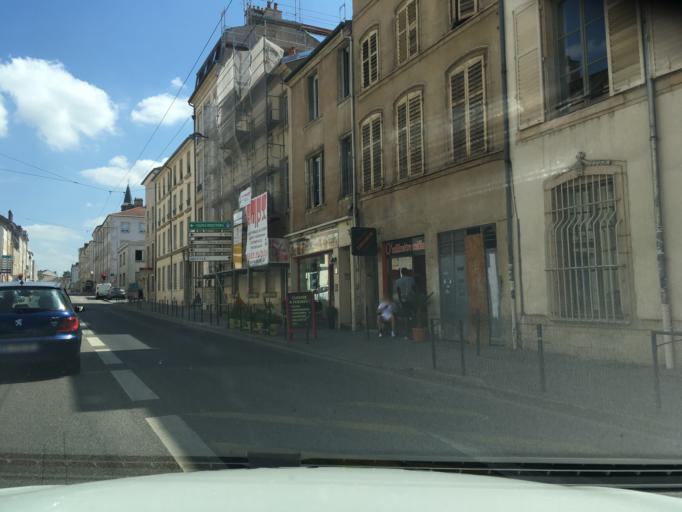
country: FR
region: Lorraine
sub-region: Departement de Meurthe-et-Moselle
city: Nancy
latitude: 48.6873
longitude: 6.1836
